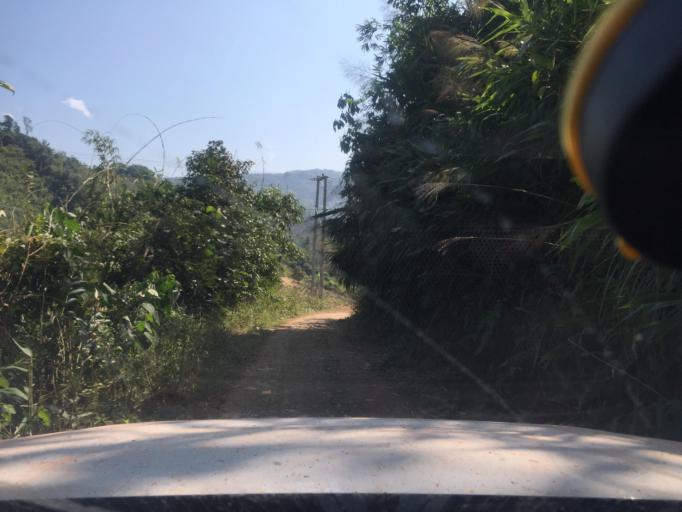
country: LA
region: Phongsali
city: Phongsali
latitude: 21.6485
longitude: 102.4111
